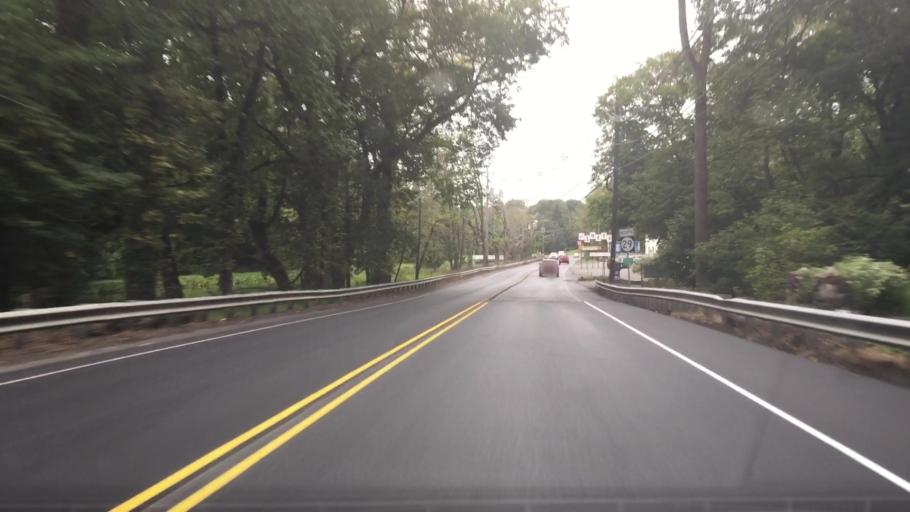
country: US
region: Pennsylvania
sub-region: Bucks County
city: Yardley
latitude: 40.3013
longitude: -74.8704
